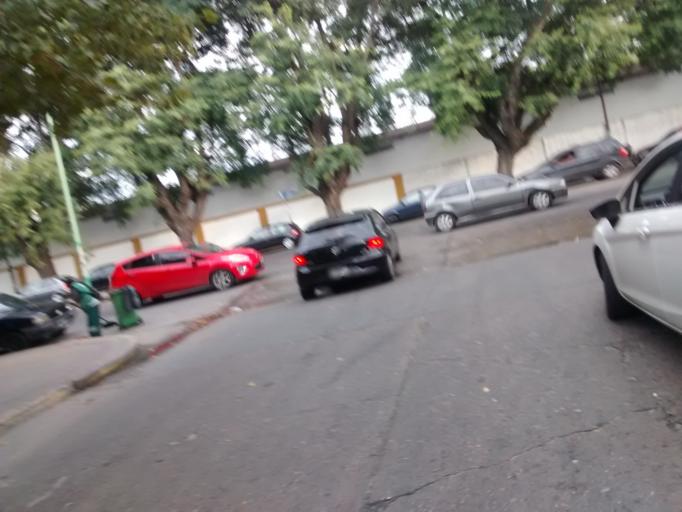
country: AR
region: Buenos Aires
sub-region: Partido de La Plata
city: La Plata
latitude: -34.9144
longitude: -57.9342
